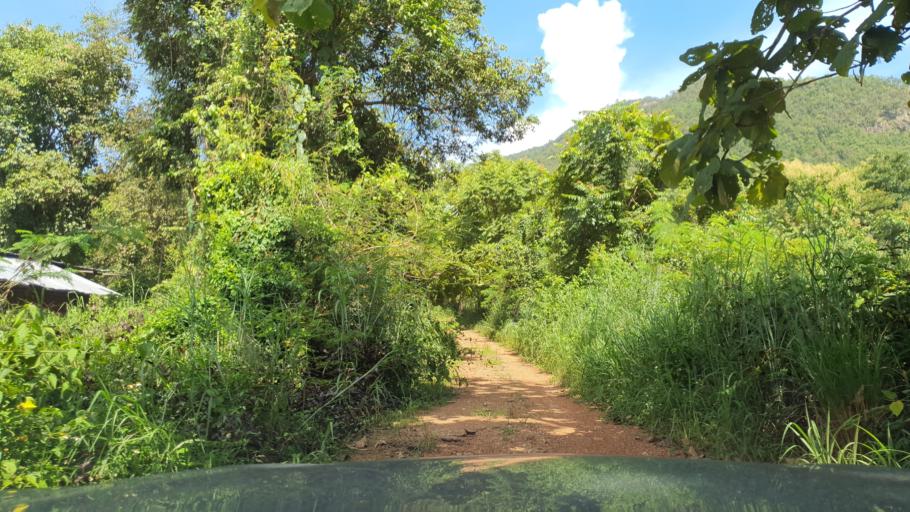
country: TH
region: Chiang Mai
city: Mae On
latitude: 18.7337
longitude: 99.2363
